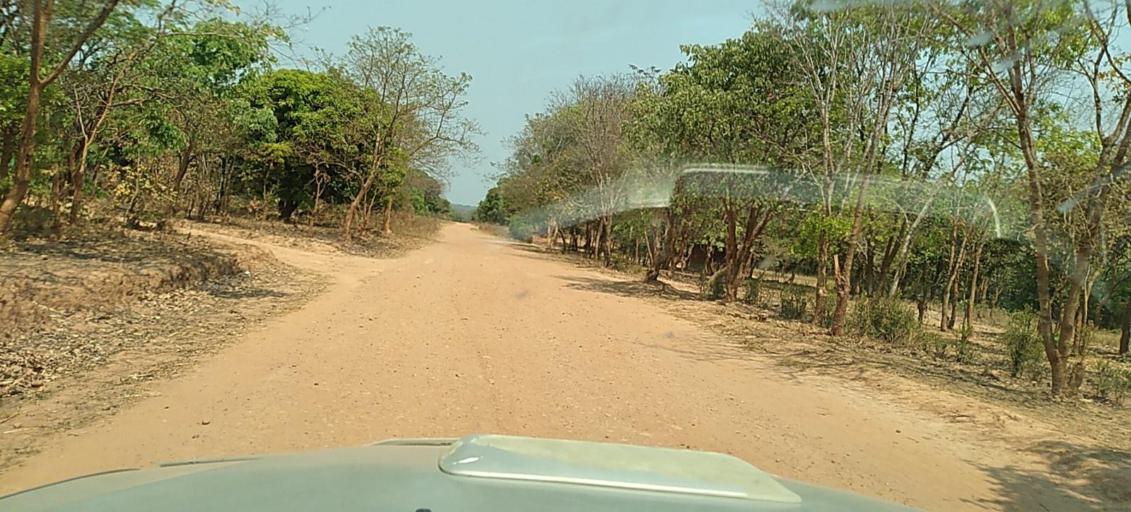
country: ZM
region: North-Western
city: Kasempa
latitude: -13.7051
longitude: 26.3344
